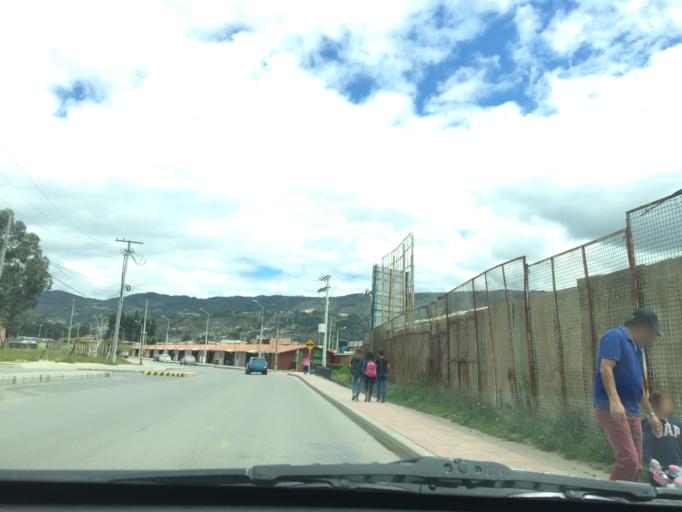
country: CO
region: Cundinamarca
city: Tocancipa
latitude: 4.9629
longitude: -73.9303
